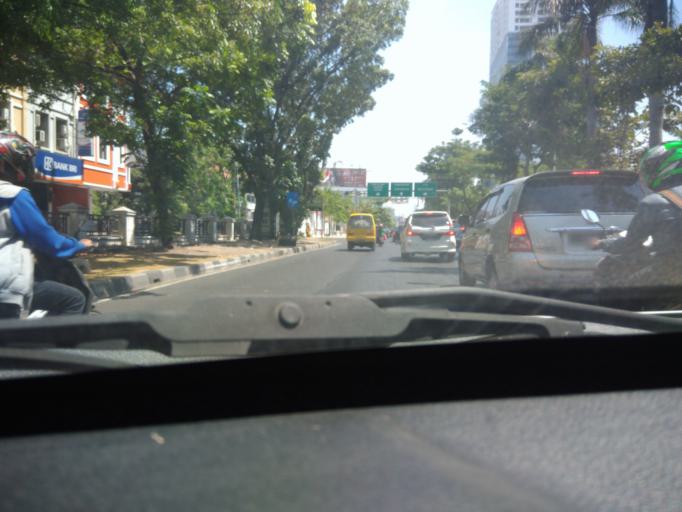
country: ID
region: East Java
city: Mulyorejo
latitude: -7.2827
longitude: 112.7808
